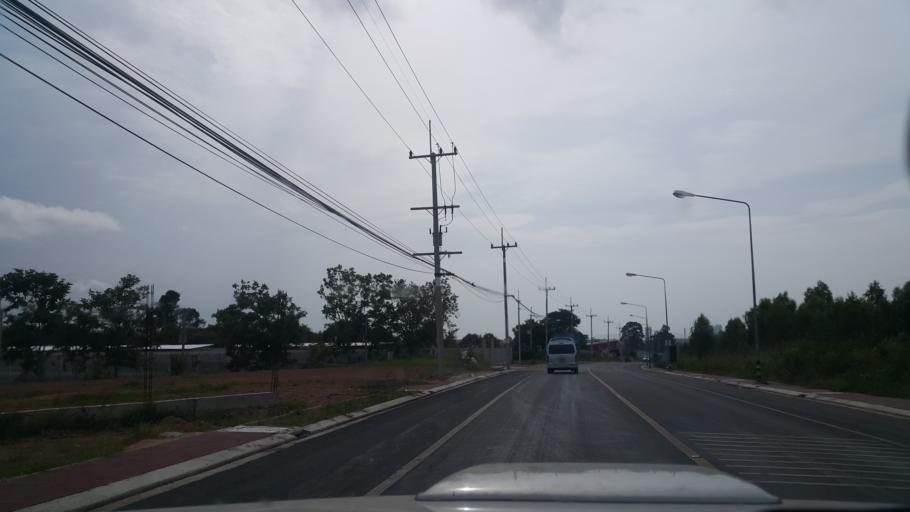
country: TH
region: Rayong
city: Ban Chang
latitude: 12.7701
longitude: 100.9525
